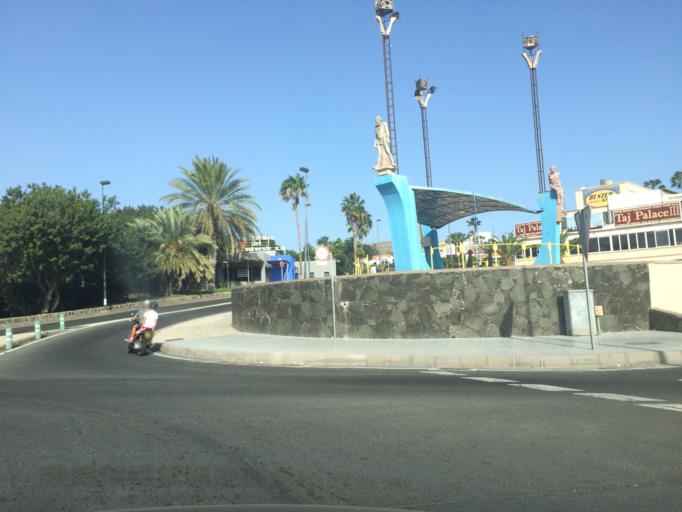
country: ES
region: Canary Islands
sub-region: Provincia de Las Palmas
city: Puerto Rico
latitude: 27.7622
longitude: -15.6835
